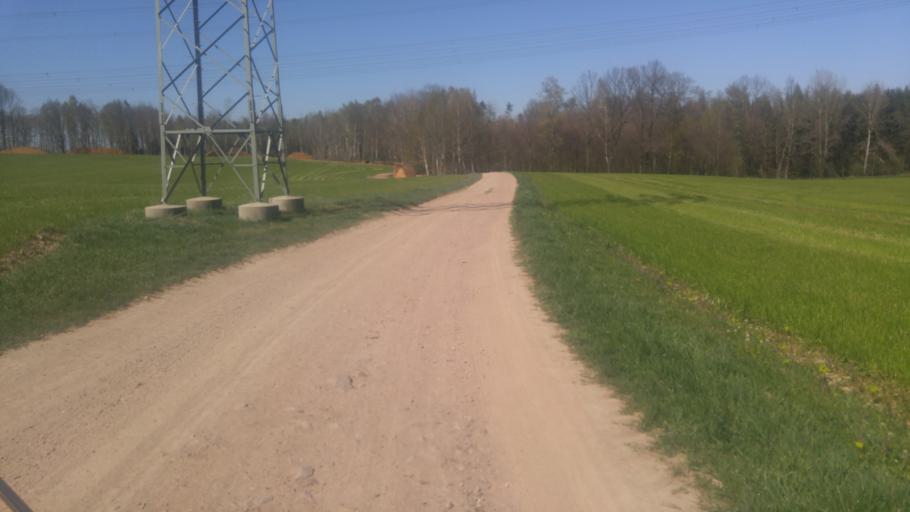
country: DE
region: Saxony
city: Altmittweida
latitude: 50.9479
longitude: 12.9627
